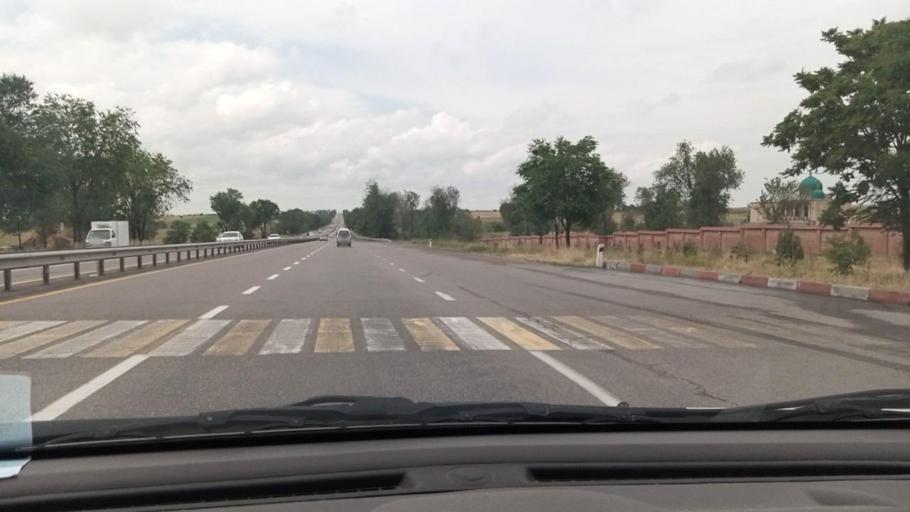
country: UZ
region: Toshkent
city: Ohangaron
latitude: 40.9959
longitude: 69.5298
